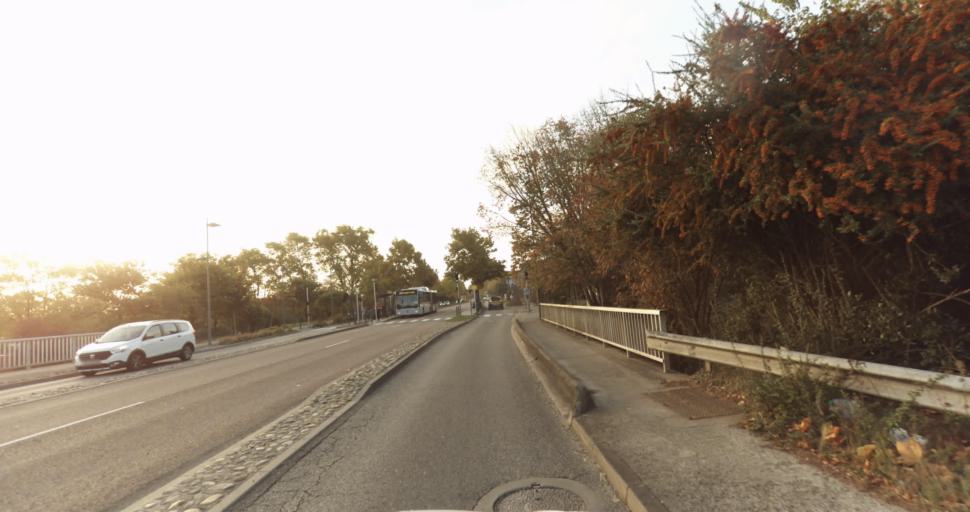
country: FR
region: Midi-Pyrenees
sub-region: Departement de la Haute-Garonne
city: Auzeville-Tolosane
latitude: 43.5348
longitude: 1.4843
